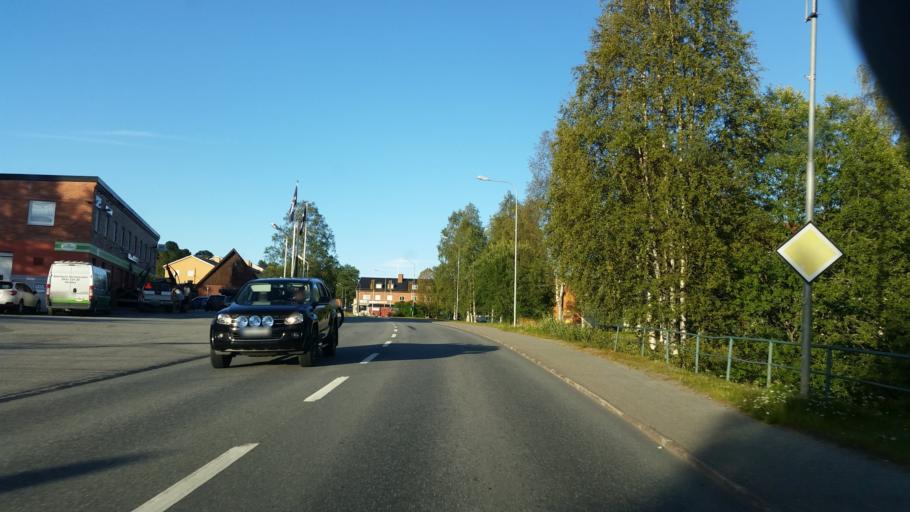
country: SE
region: Vaesterbotten
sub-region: Dorotea Kommun
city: Dorotea
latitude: 64.2604
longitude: 16.4049
